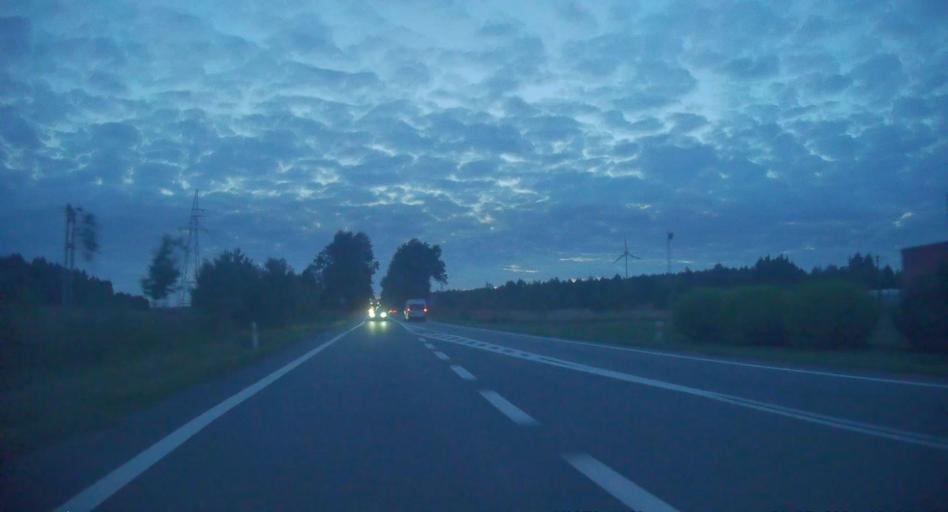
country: PL
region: Silesian Voivodeship
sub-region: Powiat klobucki
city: Klobuck
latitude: 50.9074
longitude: 18.9170
